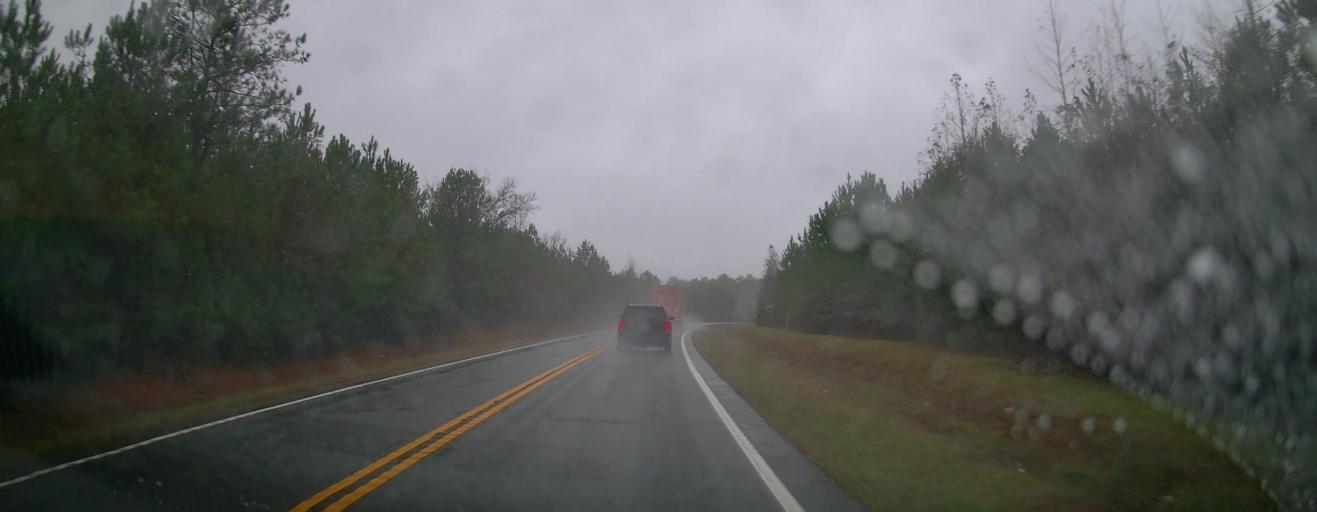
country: US
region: Georgia
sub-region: Jones County
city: Gray
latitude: 33.0988
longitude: -83.4867
